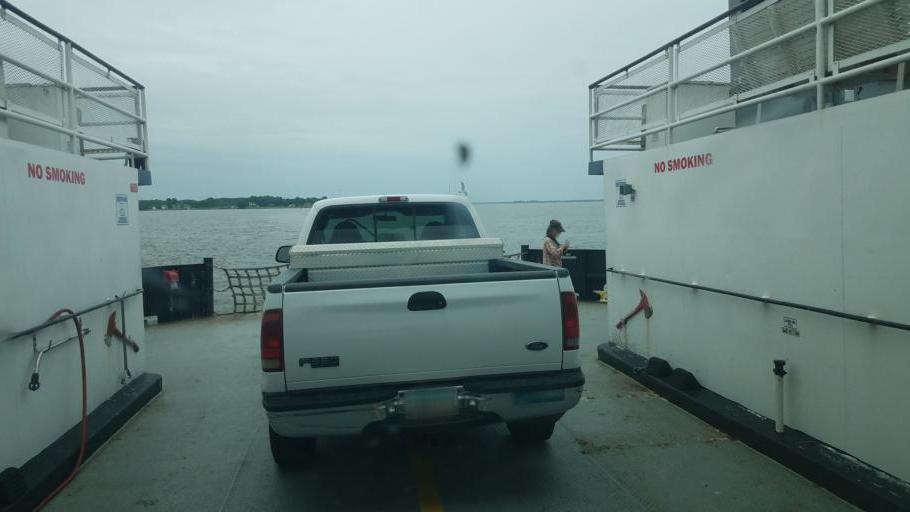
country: US
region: North Carolina
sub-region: Currituck County
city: Currituck
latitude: 36.4772
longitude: -75.9389
